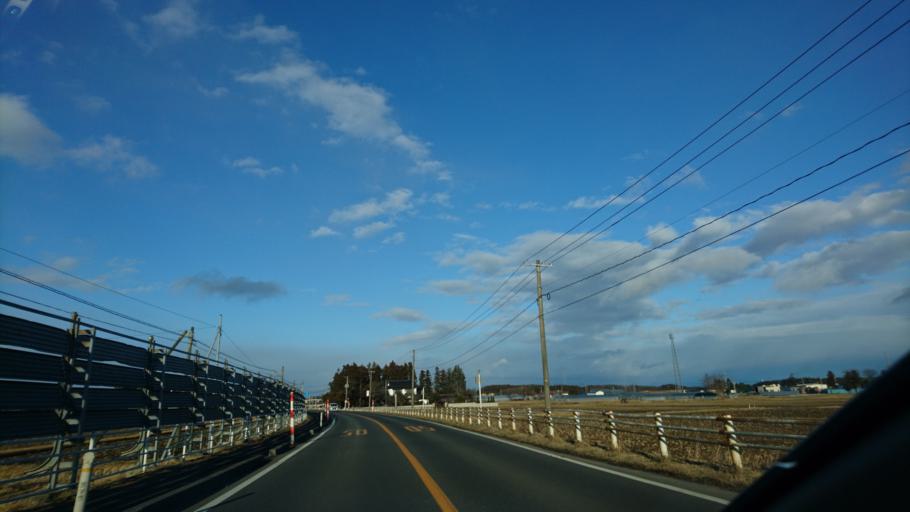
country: JP
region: Miyagi
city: Furukawa
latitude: 38.5042
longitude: 140.8655
